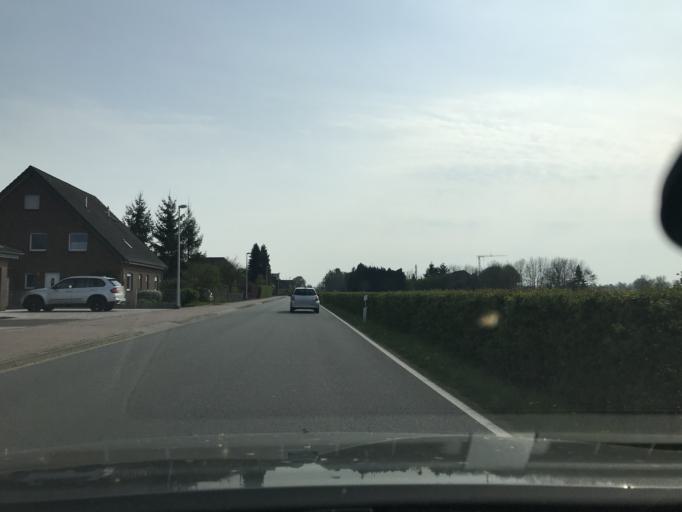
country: DE
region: North Rhine-Westphalia
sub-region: Regierungsbezirk Dusseldorf
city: Goch
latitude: 51.7219
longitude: 6.1660
